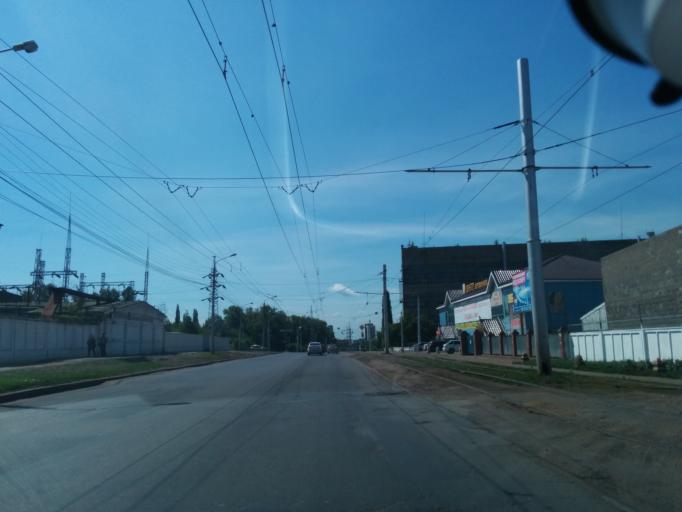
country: RU
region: Bashkortostan
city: Ufa
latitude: 54.7424
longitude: 55.9755
